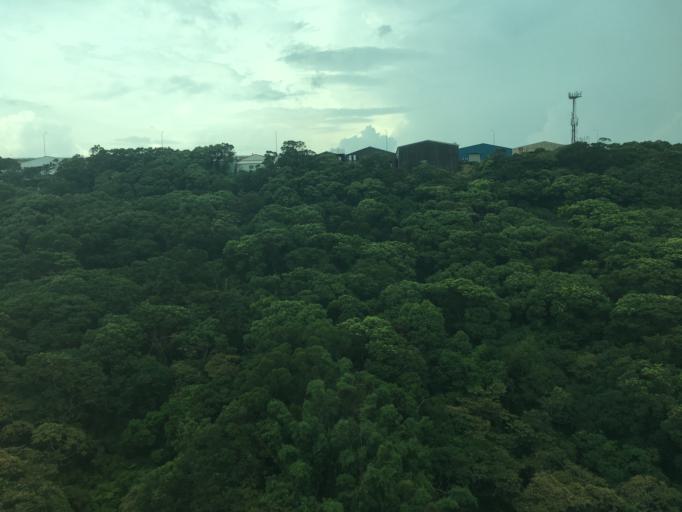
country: TW
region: Taiwan
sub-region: Taoyuan
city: Taoyuan
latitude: 25.0684
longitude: 121.3467
